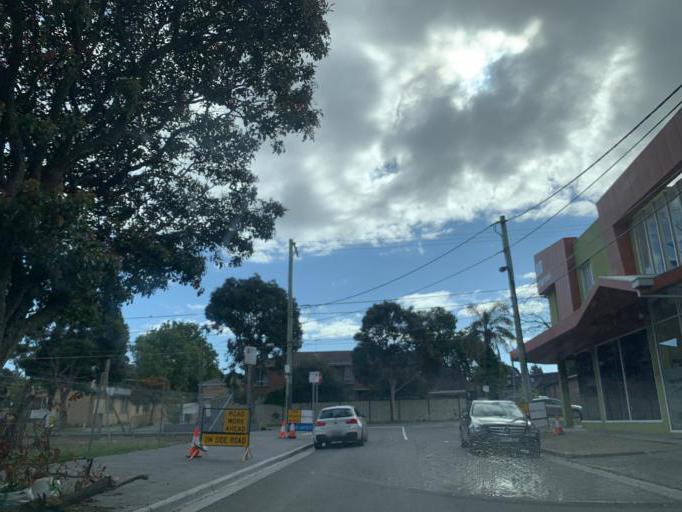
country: AU
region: Victoria
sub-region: Bayside
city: Cheltenham
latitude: -37.9692
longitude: 145.0554
